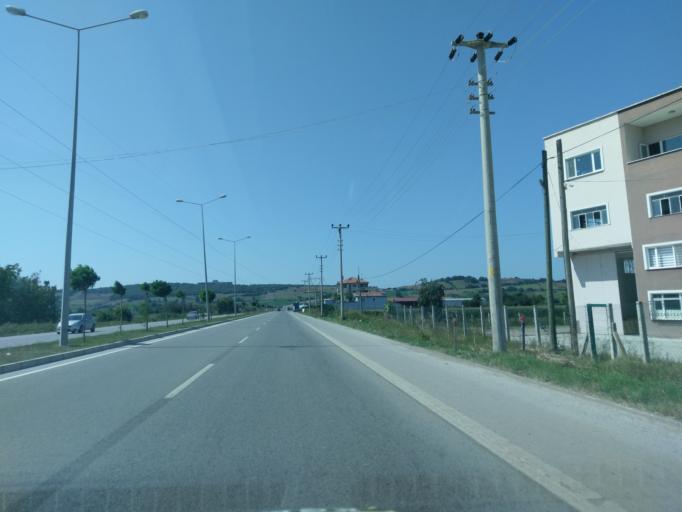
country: TR
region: Samsun
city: Bafra
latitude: 41.5760
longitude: 35.8585
